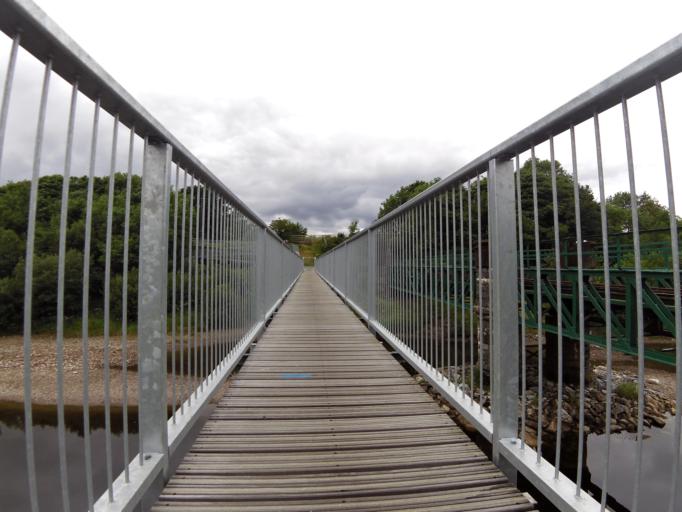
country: GB
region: Scotland
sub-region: Highland
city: Fort William
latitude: 56.8331
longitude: -5.0840
